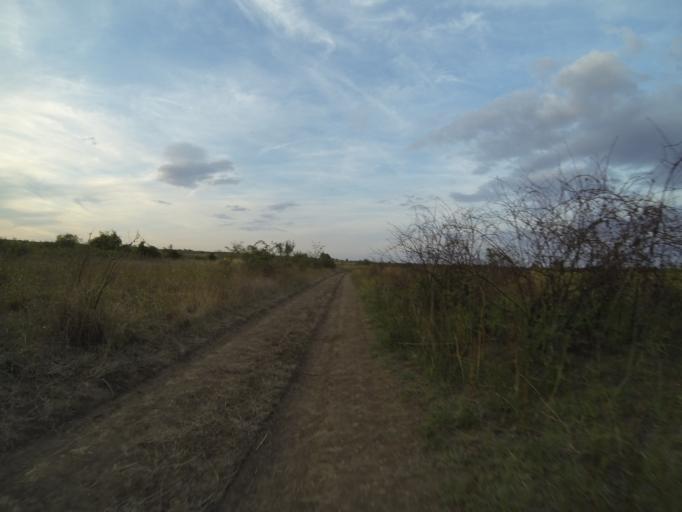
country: RO
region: Dolj
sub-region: Comuna Ceratu
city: Ceratu
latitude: 44.0997
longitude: 23.6770
